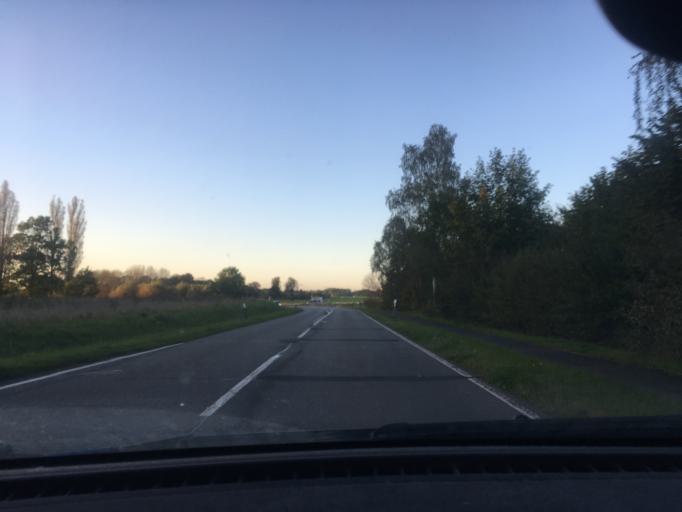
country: DE
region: Lower Saxony
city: Wendisch Evern
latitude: 53.2191
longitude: 10.4638
